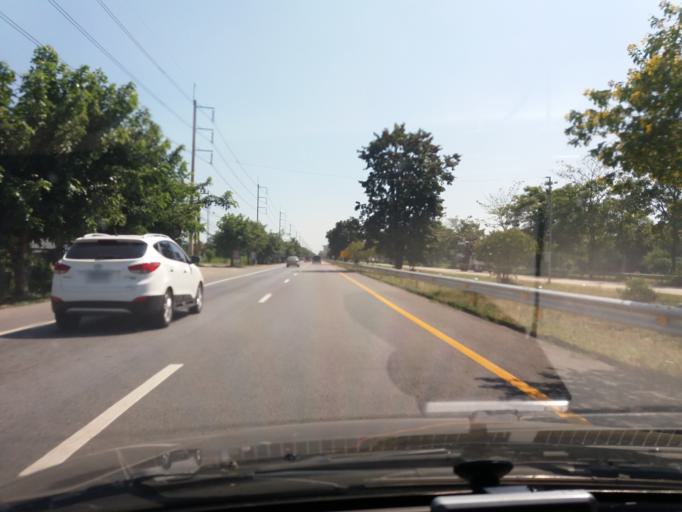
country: TH
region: Chai Nat
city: Chai Nat
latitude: 15.1328
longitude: 100.1455
